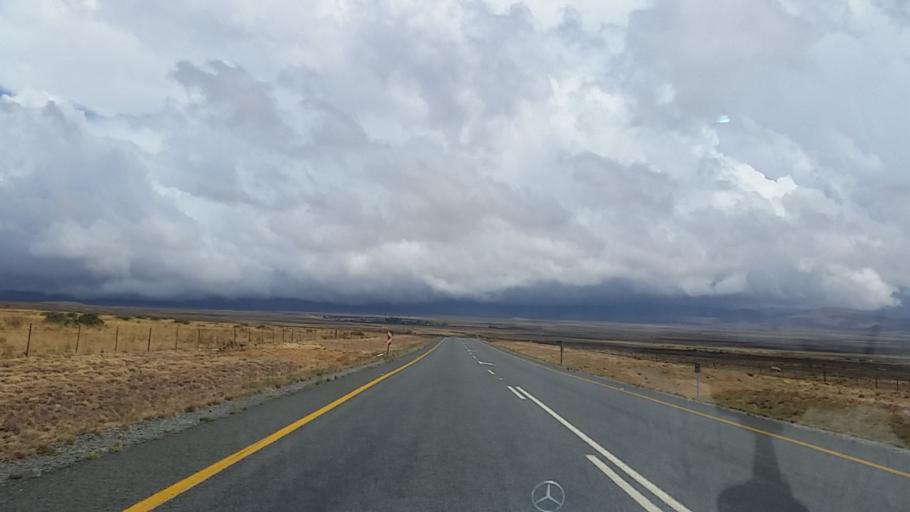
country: ZA
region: Eastern Cape
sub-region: Chris Hani District Municipality
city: Middelburg
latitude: -31.8849
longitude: 24.8117
